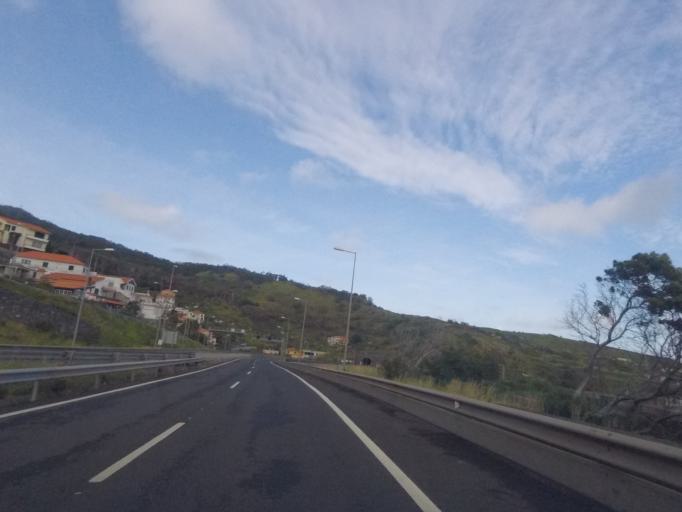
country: PT
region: Madeira
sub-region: Machico
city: Canical
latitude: 32.7424
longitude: -16.7458
